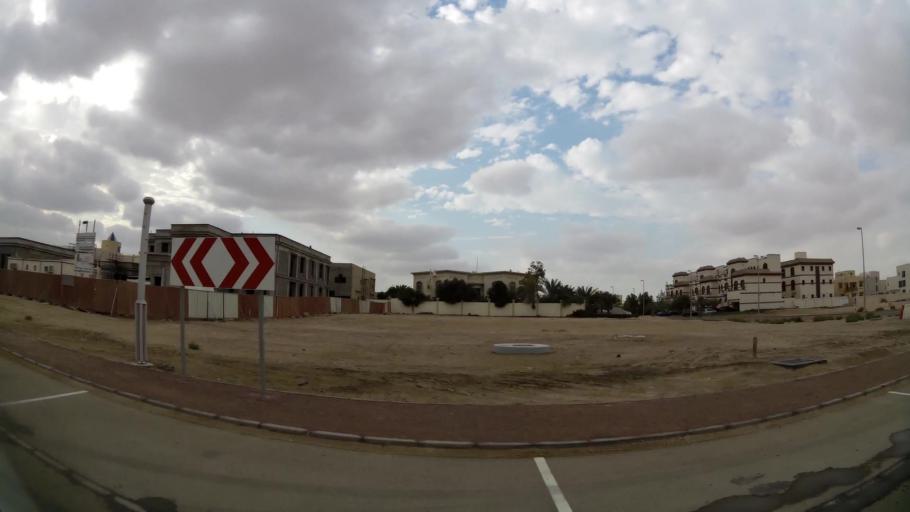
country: AE
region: Abu Dhabi
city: Abu Dhabi
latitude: 24.3507
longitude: 54.6153
